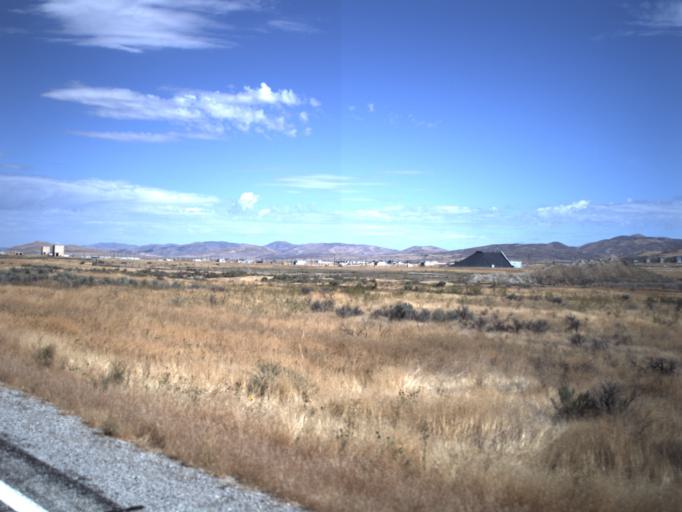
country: US
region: Utah
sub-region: Box Elder County
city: Tremonton
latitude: 41.6939
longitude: -112.4442
